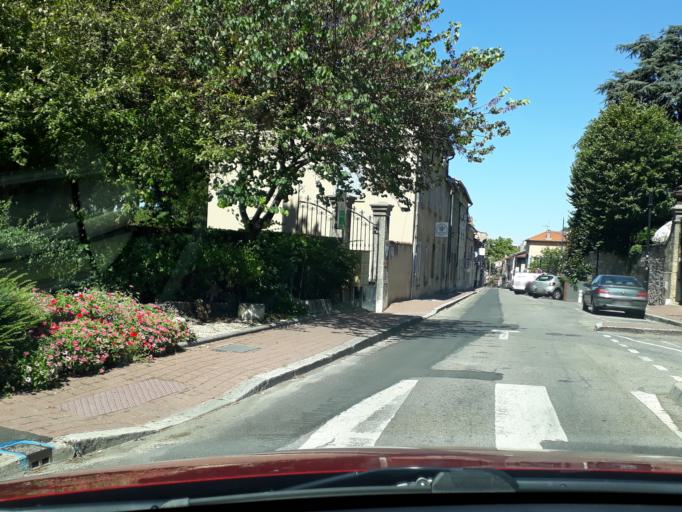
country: FR
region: Rhone-Alpes
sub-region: Departement du Rhone
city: Saint-Priest
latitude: 45.6975
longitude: 4.9437
